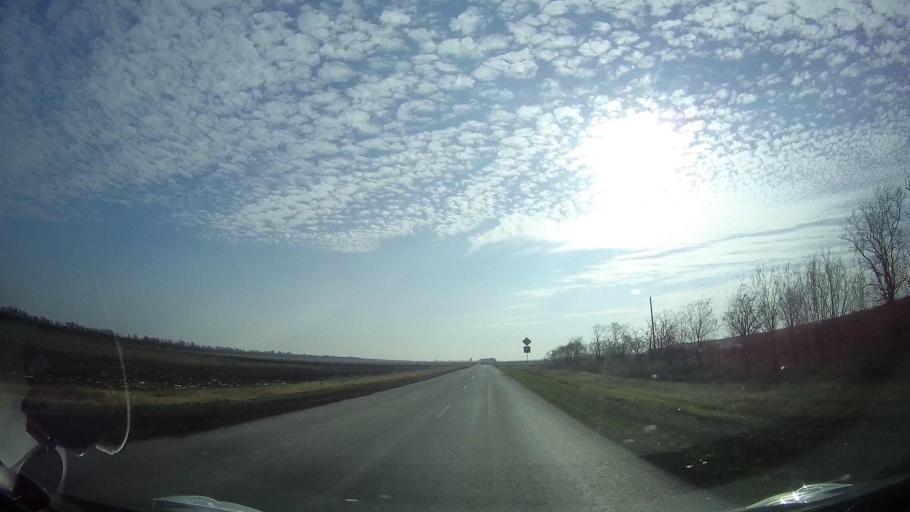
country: RU
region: Rostov
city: Veselyy
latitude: 46.9729
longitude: 40.7195
